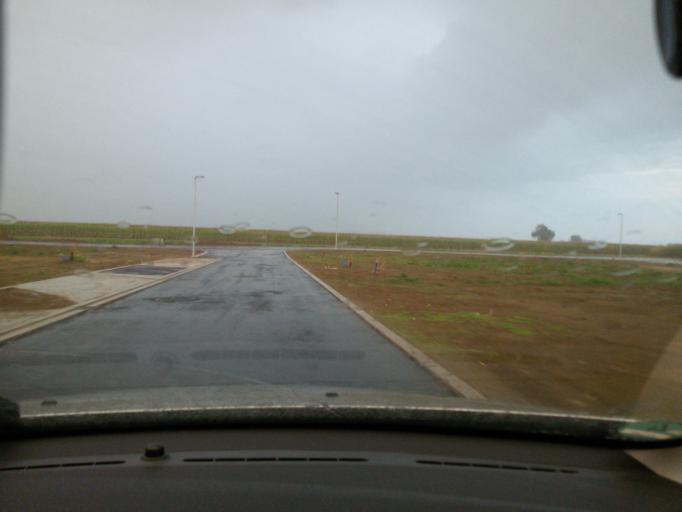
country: DE
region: Bavaria
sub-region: Swabia
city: Hiltenfingen
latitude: 48.1599
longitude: 10.7257
